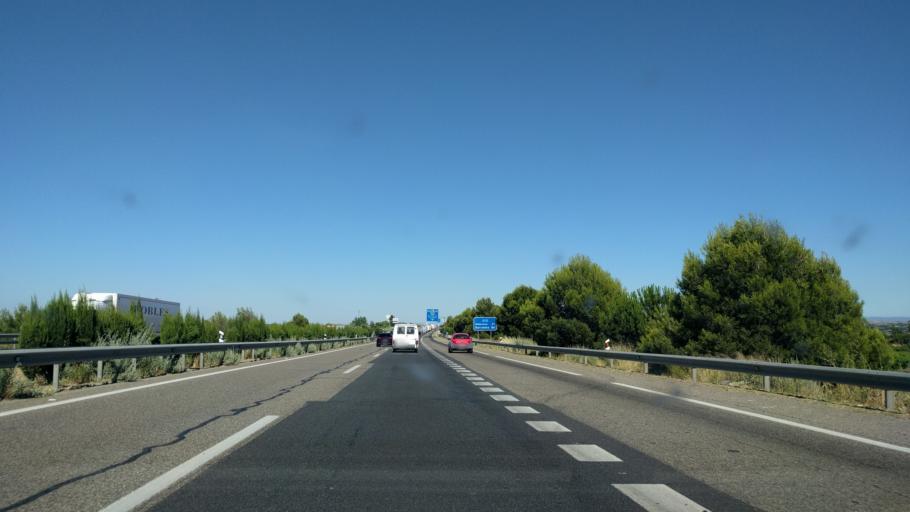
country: ES
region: Catalonia
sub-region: Provincia de Lleida
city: Torrefarrera
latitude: 41.6637
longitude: 0.6165
